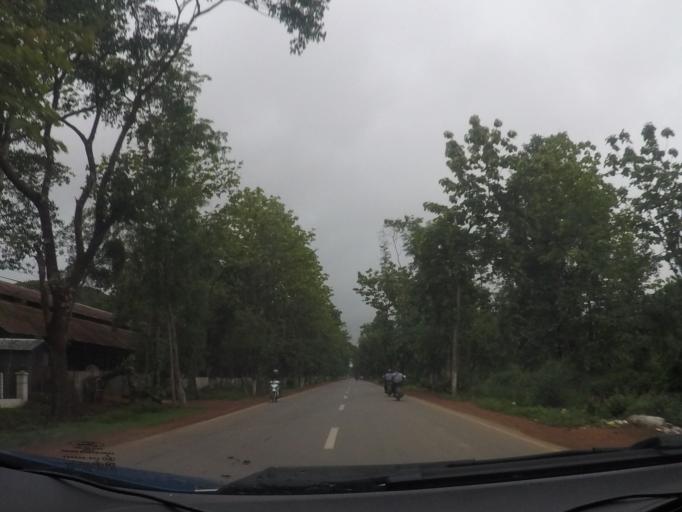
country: MM
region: Bago
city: Paungde
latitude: 18.2412
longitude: 95.6461
